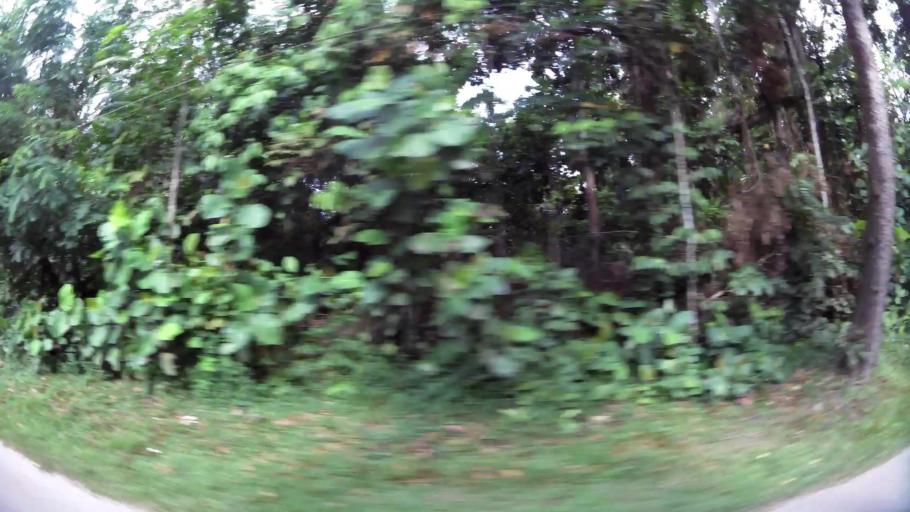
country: MY
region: Johor
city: Johor Bahru
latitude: 1.4077
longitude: 103.7016
